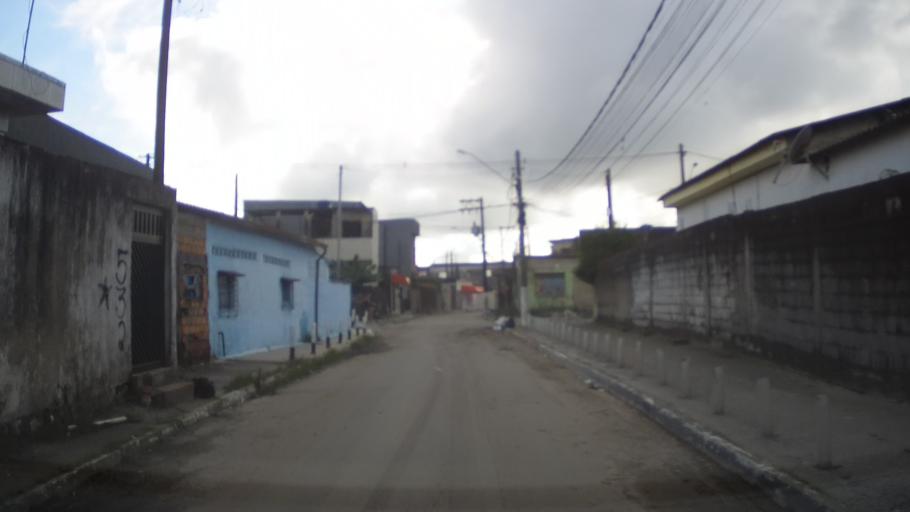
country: BR
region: Sao Paulo
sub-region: Praia Grande
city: Praia Grande
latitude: -24.0118
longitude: -46.4734
